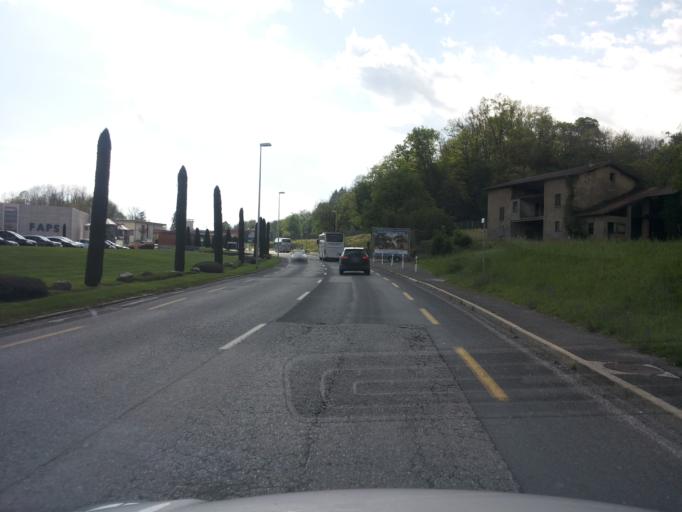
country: CH
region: Ticino
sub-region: Mendrisio District
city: Stabio
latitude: 45.8448
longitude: 8.9248
